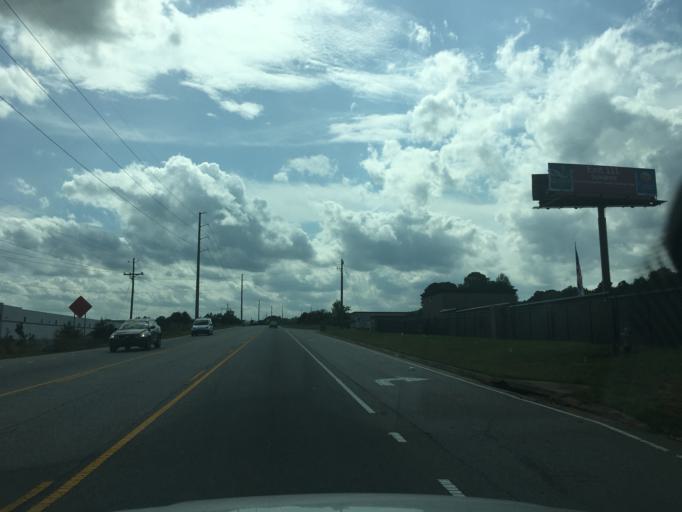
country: US
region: Georgia
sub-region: Jackson County
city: Hoschton
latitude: 34.0989
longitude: -83.7963
